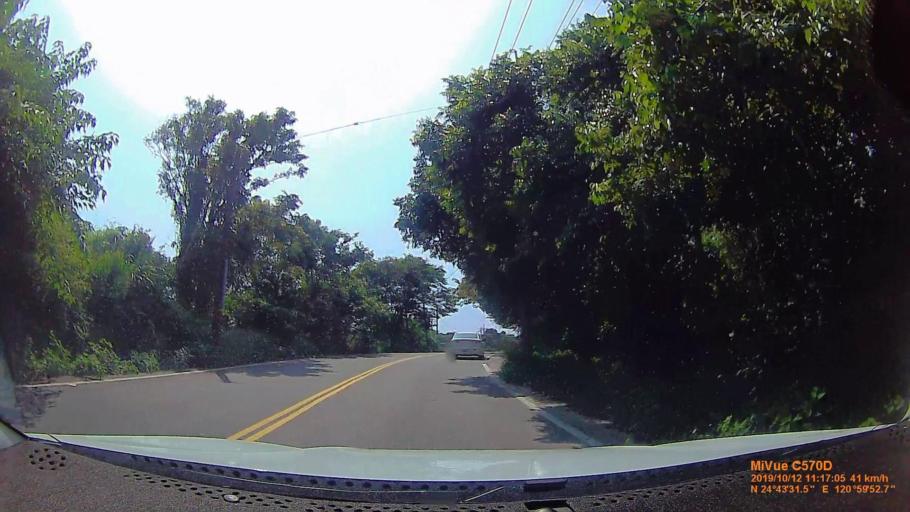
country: TW
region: Taiwan
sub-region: Hsinchu
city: Hsinchu
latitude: 24.7253
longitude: 120.9980
